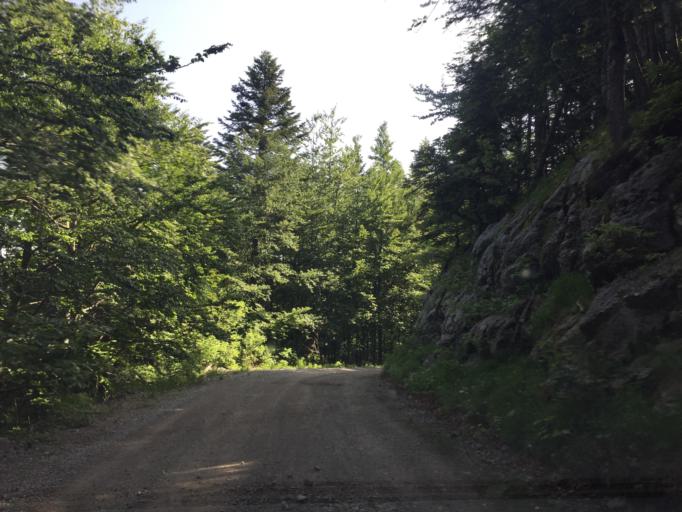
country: HR
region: Primorsko-Goranska
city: Podhum
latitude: 45.4526
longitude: 14.5471
